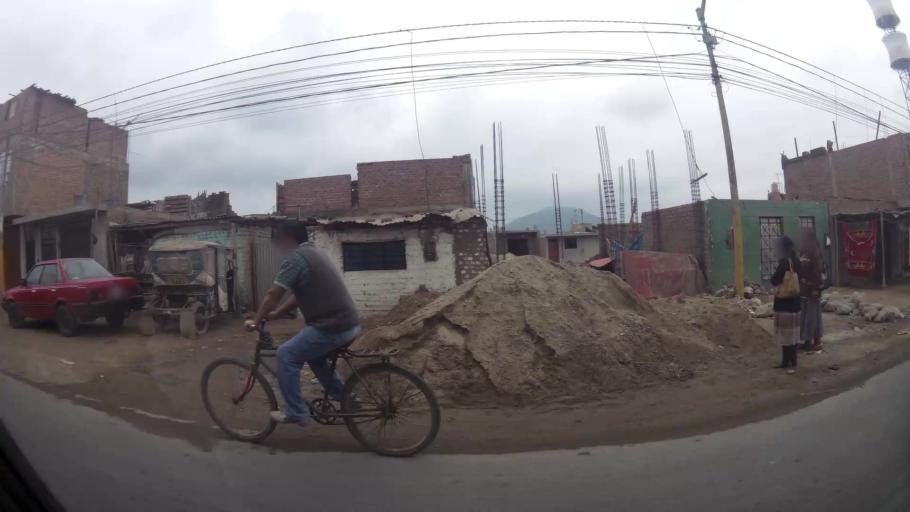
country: PE
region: Lima
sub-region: Provincia de Huaral
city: Huaral
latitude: -11.5008
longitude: -77.2231
